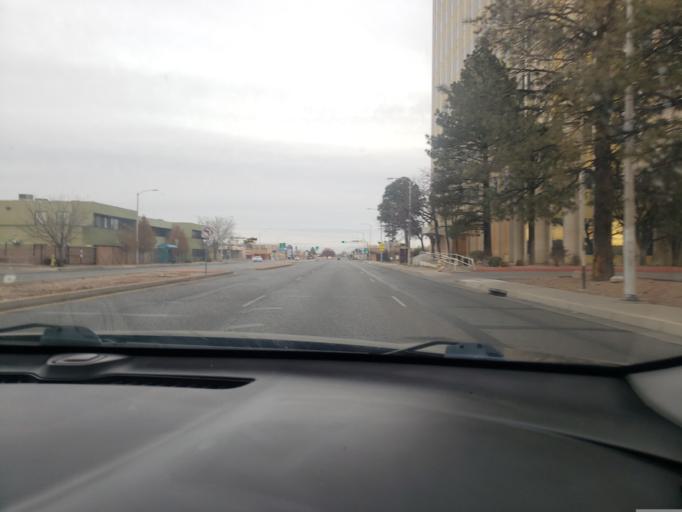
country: US
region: New Mexico
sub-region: Bernalillo County
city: Albuquerque
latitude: 35.0792
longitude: -106.5860
